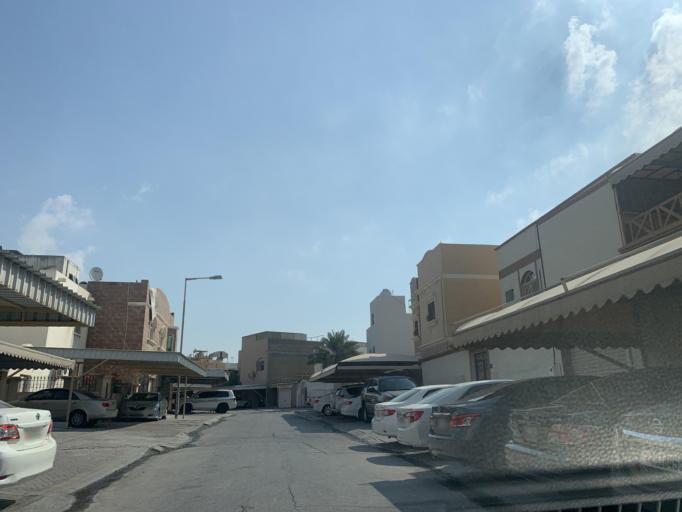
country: BH
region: Central Governorate
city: Madinat Hamad
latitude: 26.1046
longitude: 50.4990
